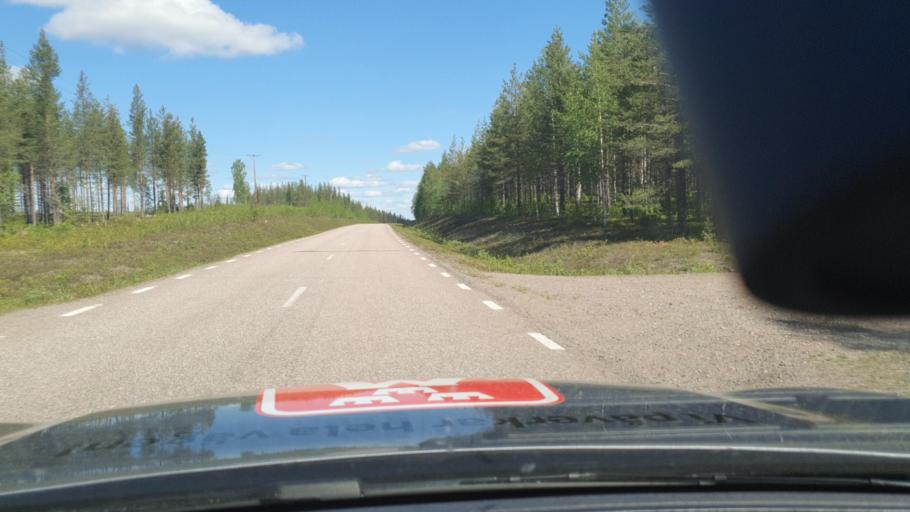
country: SE
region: Norrbotten
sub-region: Overkalix Kommun
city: OEverkalix
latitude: 67.0432
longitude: 22.5019
